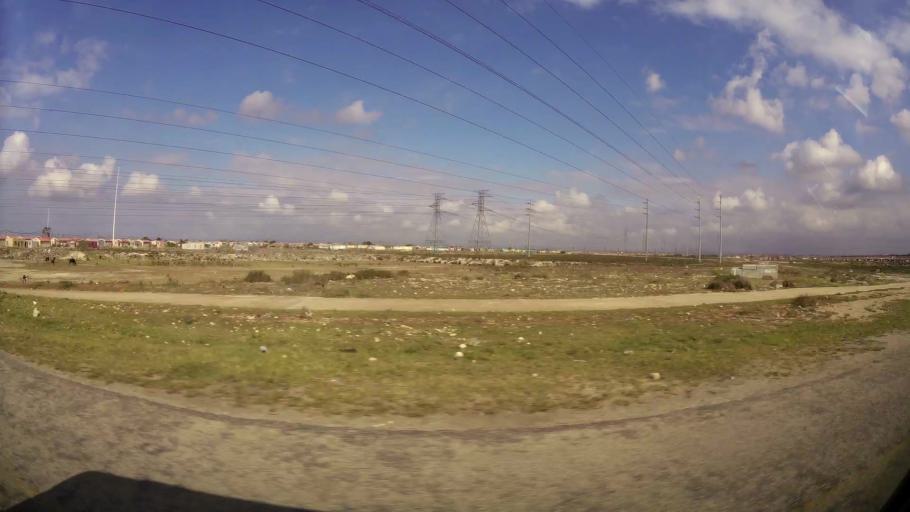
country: ZA
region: Eastern Cape
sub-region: Nelson Mandela Bay Metropolitan Municipality
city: Port Elizabeth
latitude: -33.7708
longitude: 25.5795
